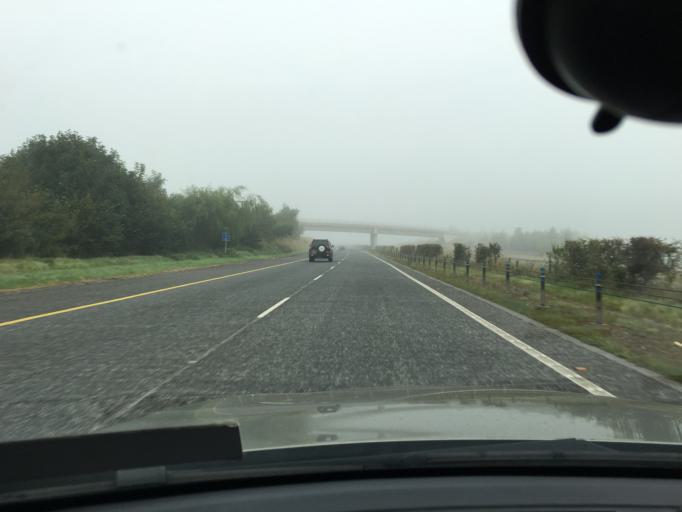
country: IE
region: Leinster
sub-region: An Mhi
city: Longwood
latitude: 53.4339
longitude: -6.9991
